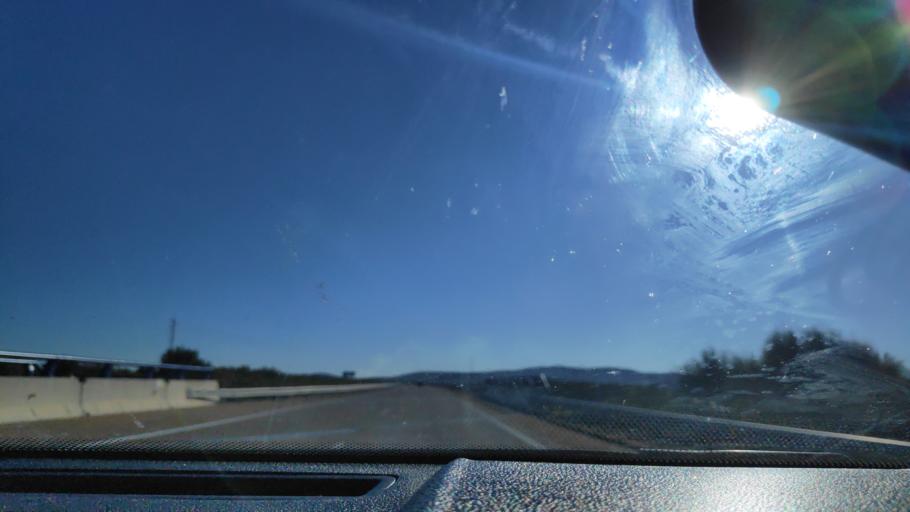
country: ES
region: Extremadura
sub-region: Provincia de Badajoz
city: Villafranca de los Barros
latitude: 38.5515
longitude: -6.3639
